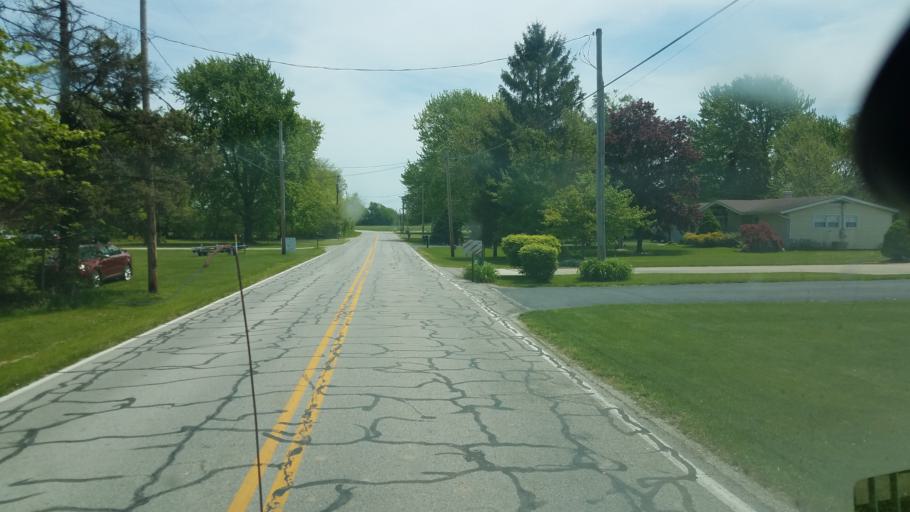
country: US
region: Ohio
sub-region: Ottawa County
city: Oak Harbor
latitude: 41.4972
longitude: -83.1766
